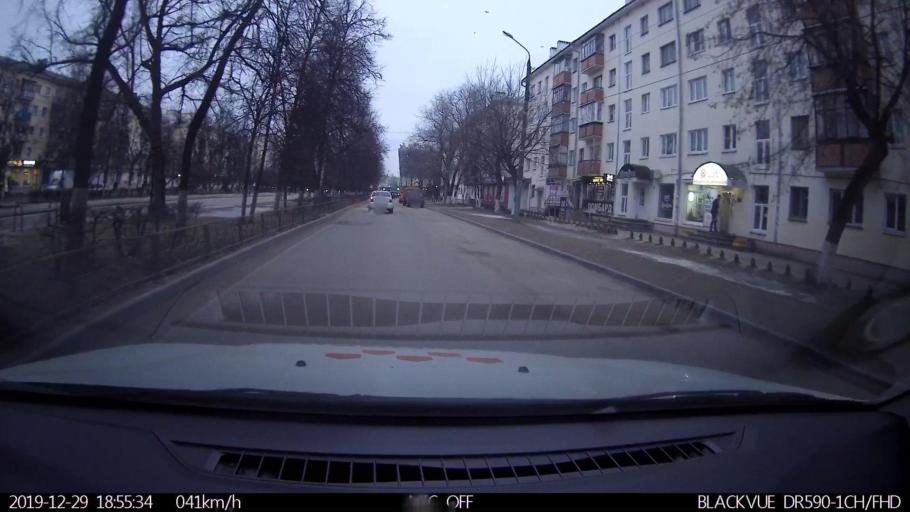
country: RU
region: Nizjnij Novgorod
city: Neklyudovo
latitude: 56.3464
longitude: 43.8663
